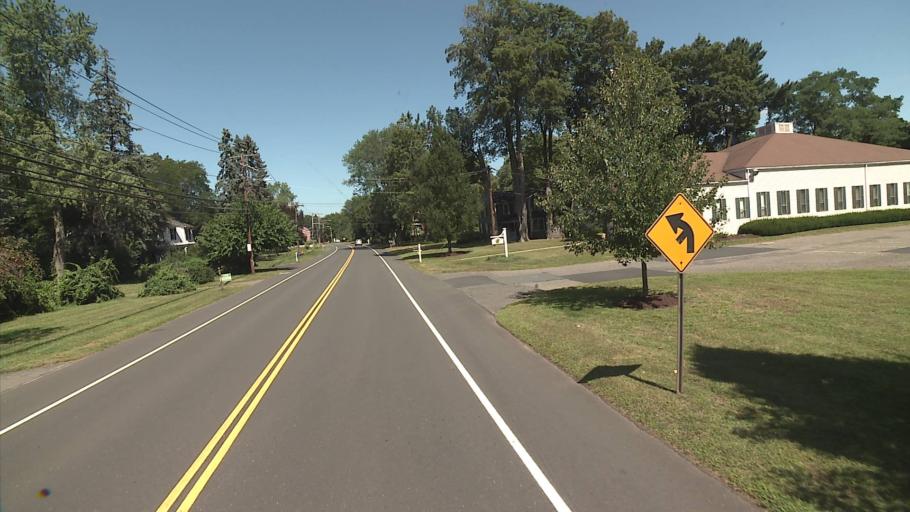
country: US
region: Connecticut
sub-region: Hartford County
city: Windsor
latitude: 41.8649
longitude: -72.6305
